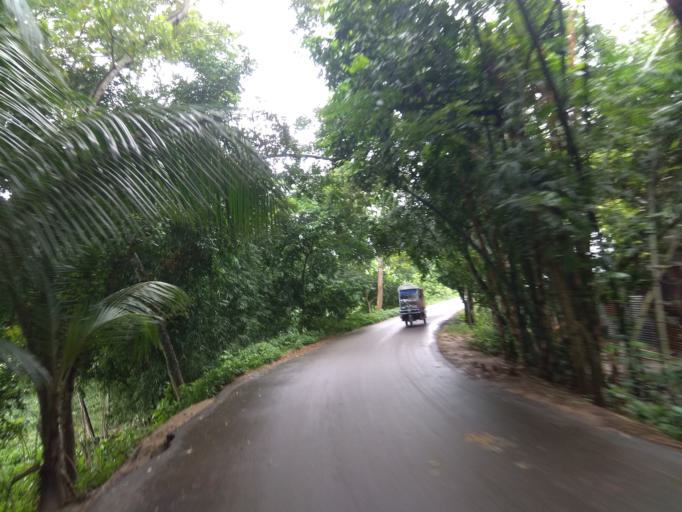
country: BD
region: Dhaka
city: Dohar
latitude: 23.4333
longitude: 90.0731
